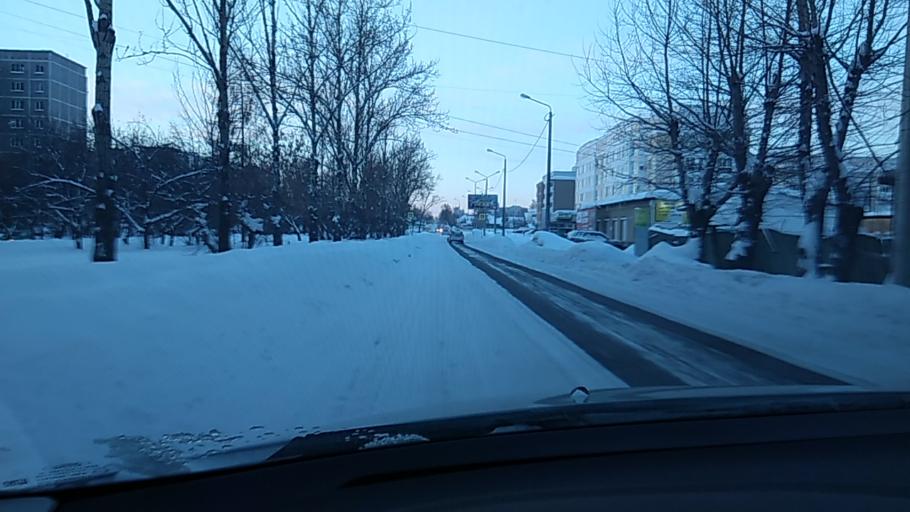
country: RU
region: Sverdlovsk
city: Sovkhoznyy
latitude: 56.8043
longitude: 60.5791
